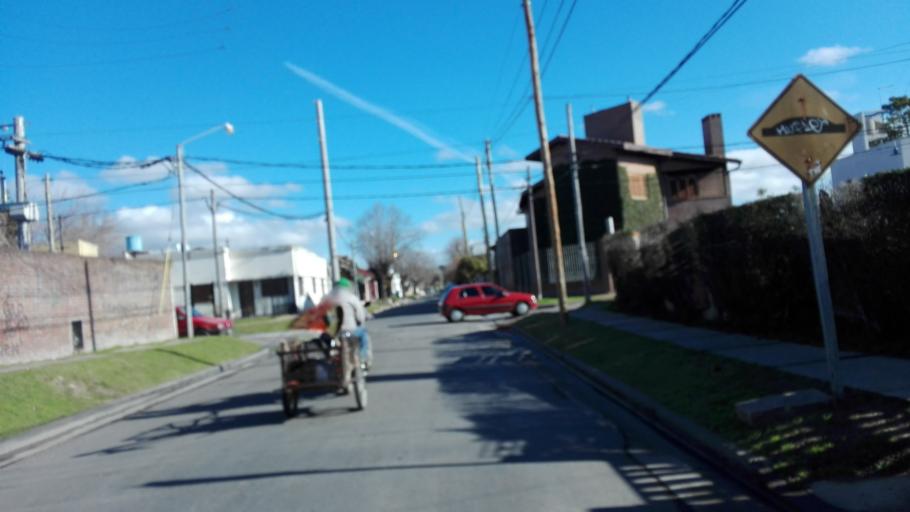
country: AR
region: Buenos Aires
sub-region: Partido de La Plata
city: La Plata
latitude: -34.8826
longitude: -57.9944
